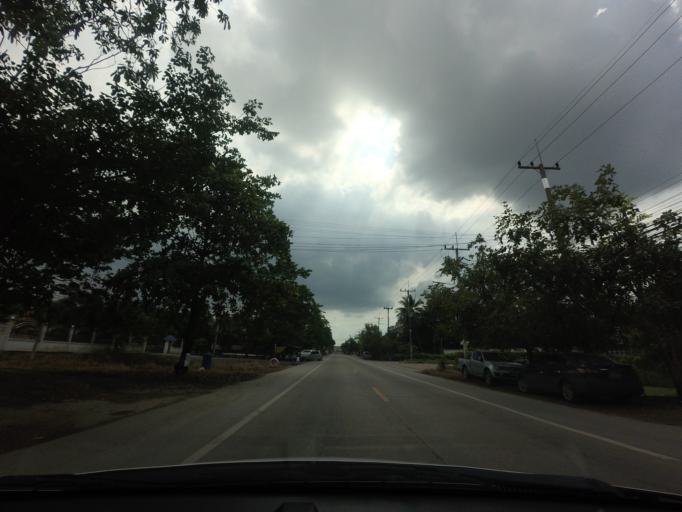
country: TH
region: Nakhon Pathom
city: Sam Phran
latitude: 13.7548
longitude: 100.2305
